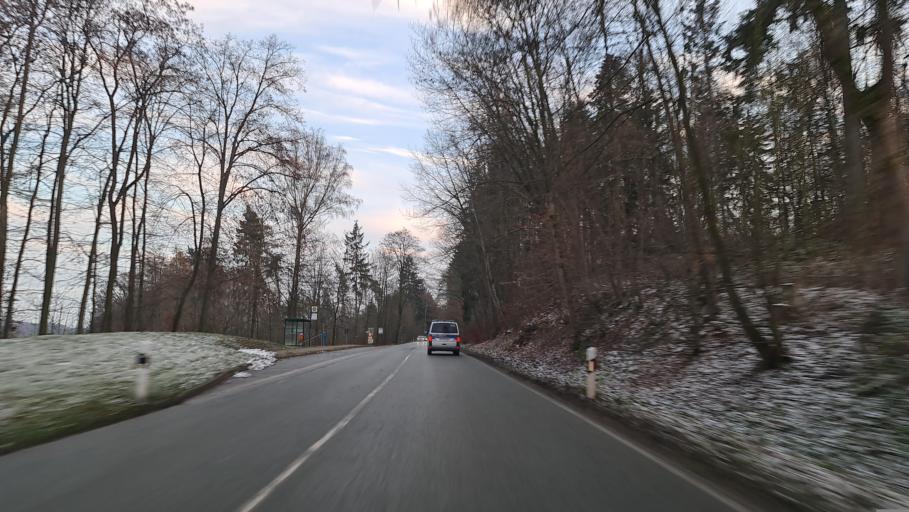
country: DE
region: Saxony
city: Pohl
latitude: 50.5457
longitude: 12.1794
